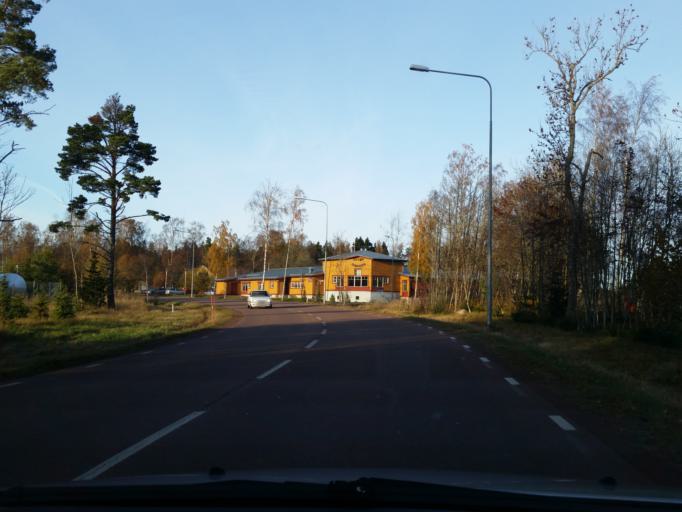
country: AX
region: Mariehamns stad
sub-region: Mariehamn
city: Mariehamn
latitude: 60.1204
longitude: 19.9165
